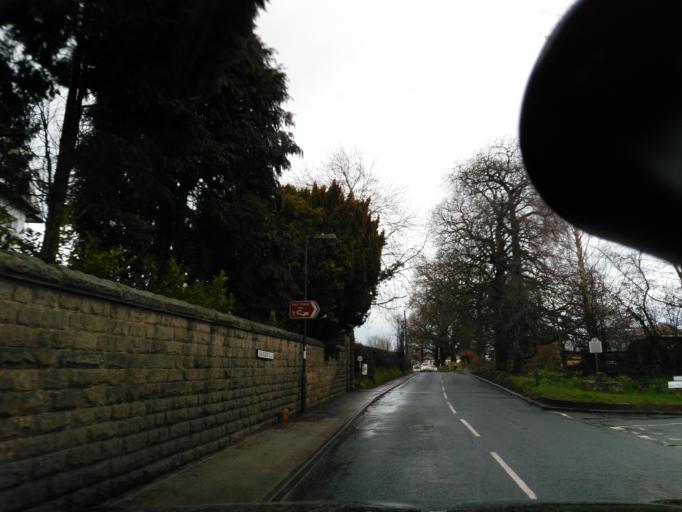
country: GB
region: England
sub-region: North Yorkshire
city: Ripon
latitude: 54.1427
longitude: -1.5067
